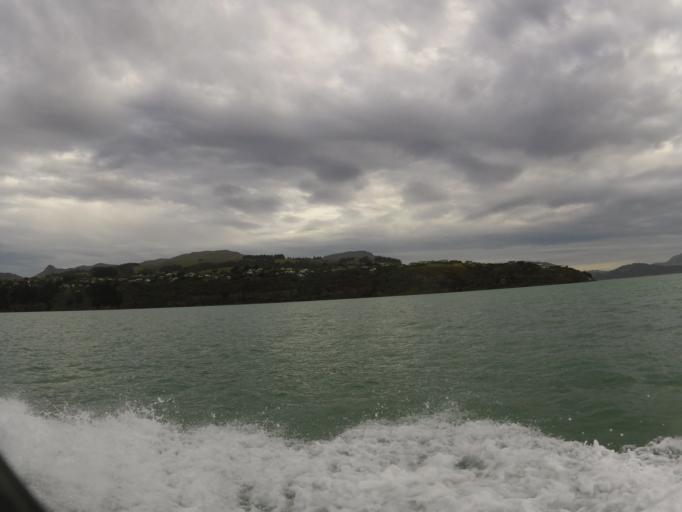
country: NZ
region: Canterbury
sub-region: Christchurch City
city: Christchurch
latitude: -43.6176
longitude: 172.7262
